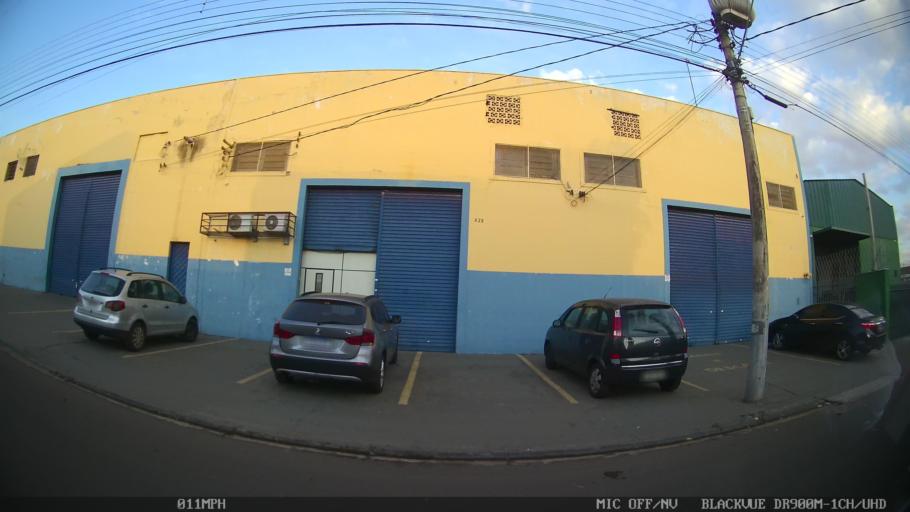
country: BR
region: Sao Paulo
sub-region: Ribeirao Preto
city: Ribeirao Preto
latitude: -21.1450
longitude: -47.7923
